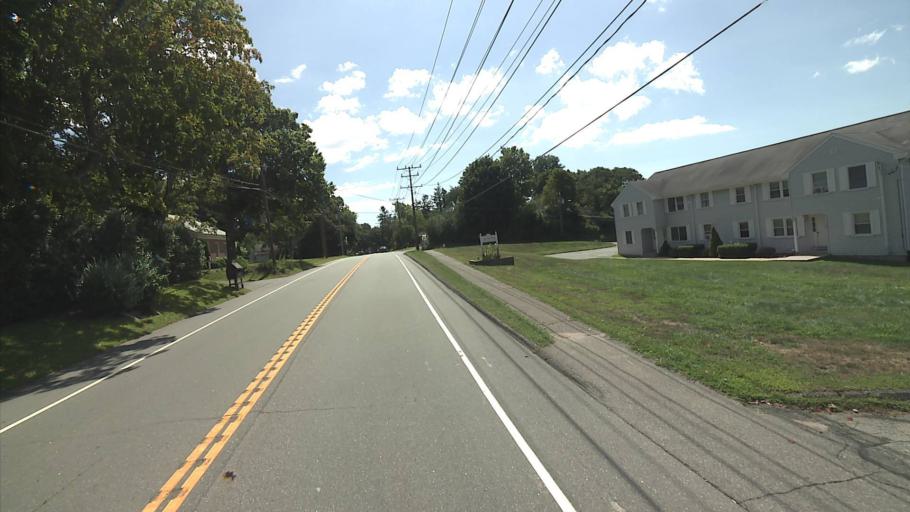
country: US
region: Connecticut
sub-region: Middlesex County
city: Westbrook Center
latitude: 41.2828
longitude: -72.4399
